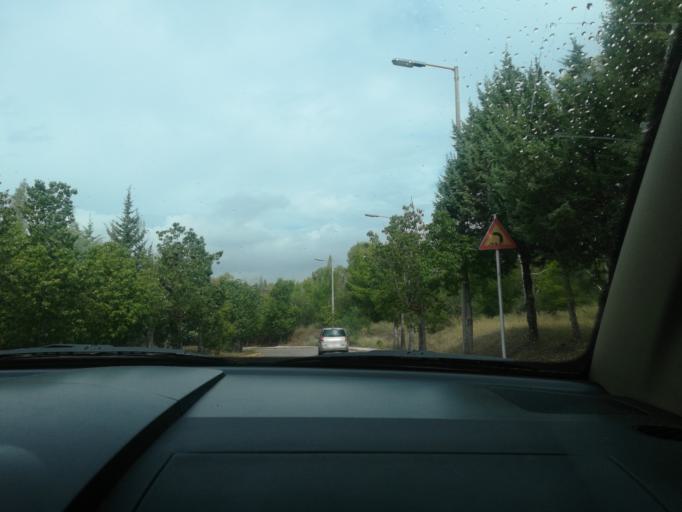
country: GR
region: Attica
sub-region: Nomos Attikis
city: Zografos
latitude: 37.9815
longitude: 23.7820
